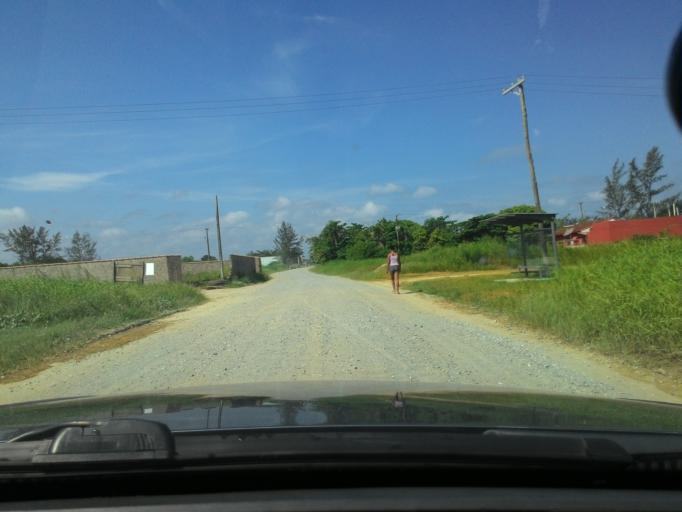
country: BR
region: Sao Paulo
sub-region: Iguape
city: Iguape
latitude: -24.8467
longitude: -47.6935
